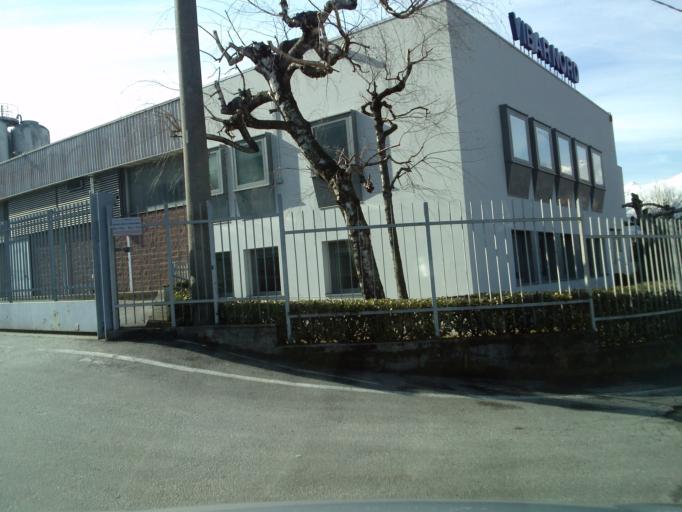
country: IT
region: Lombardy
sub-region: Provincia di Lecco
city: Colico Piano
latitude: 46.1378
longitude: 9.3909
